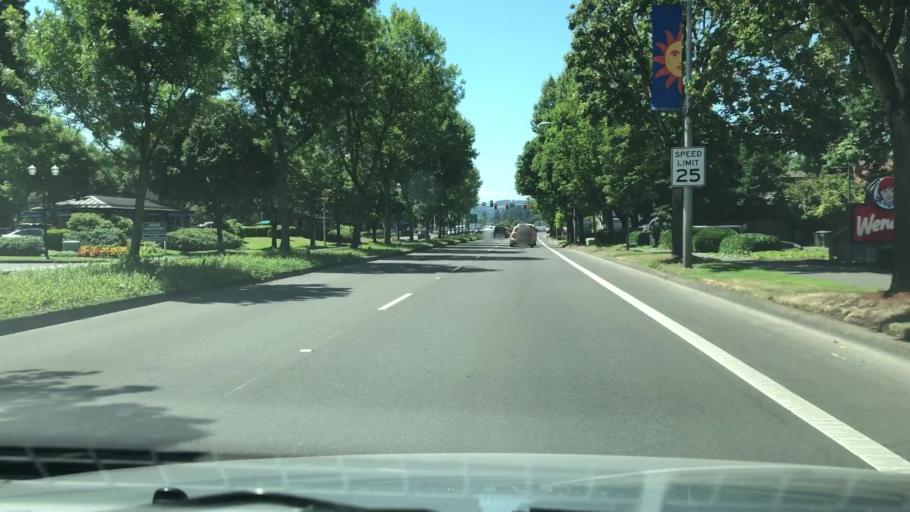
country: US
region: Oregon
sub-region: Clackamas County
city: Wilsonville
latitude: 45.3030
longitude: -122.7635
